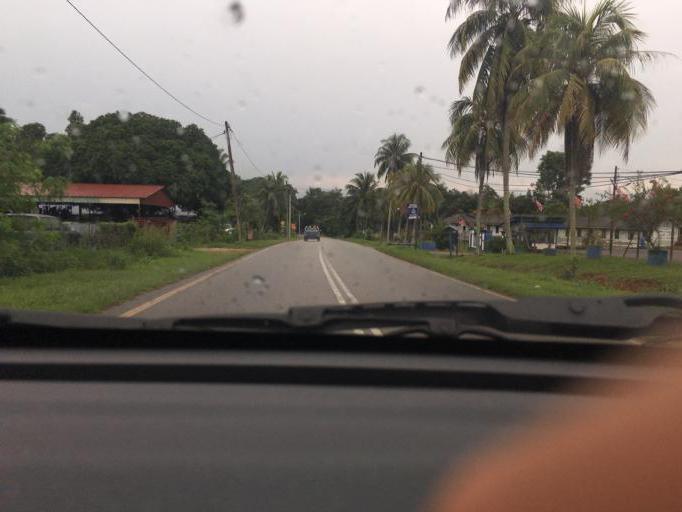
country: MY
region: Kedah
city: Bedong
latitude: 5.6960
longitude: 100.6330
